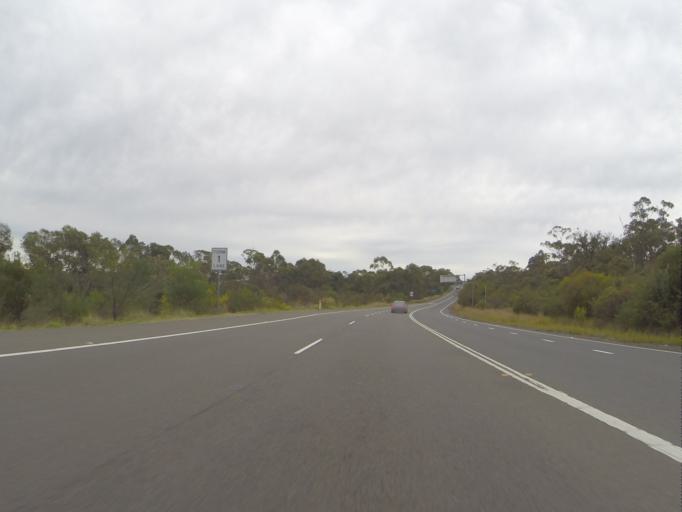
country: AU
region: New South Wales
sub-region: Sutherland Shire
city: Engadine
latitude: -34.0530
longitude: 150.9718
